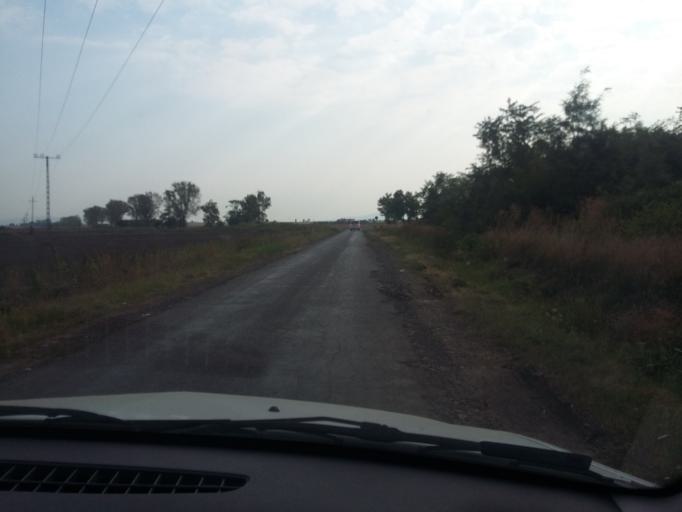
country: HU
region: Borsod-Abauj-Zemplen
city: Taktaharkany
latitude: 48.1206
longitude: 21.1135
